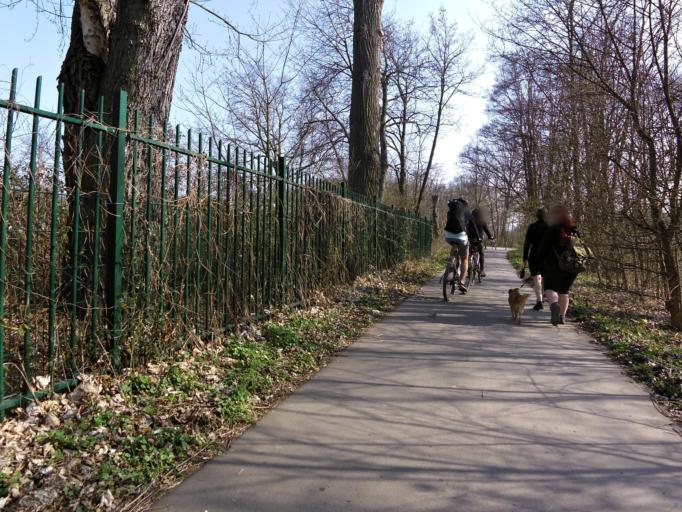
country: DE
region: Saxony
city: Leipzig
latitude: 51.3559
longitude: 12.3392
